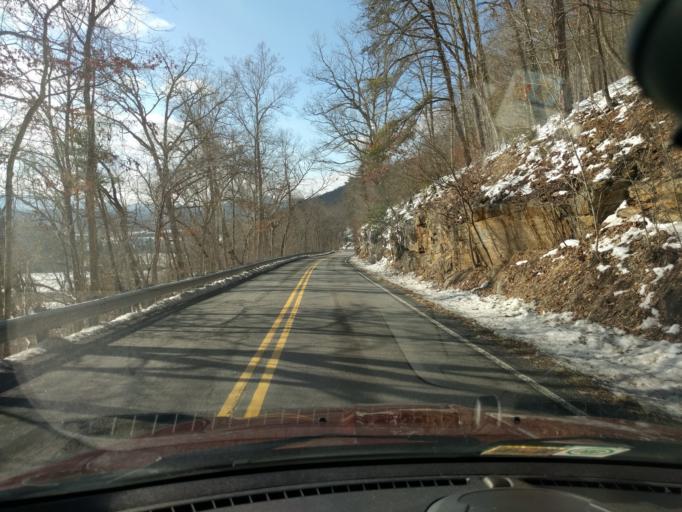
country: US
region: Virginia
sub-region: Bath County
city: Warm Springs
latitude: 38.0839
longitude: -79.8426
